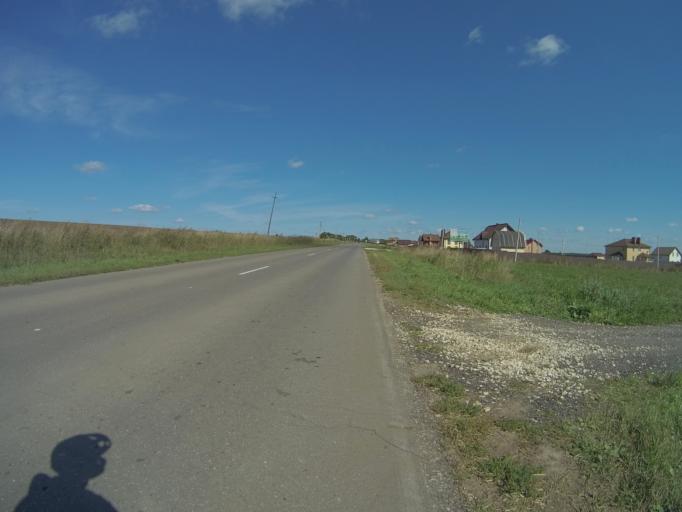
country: RU
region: Vladimir
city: Bogolyubovo
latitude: 56.2943
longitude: 40.5521
